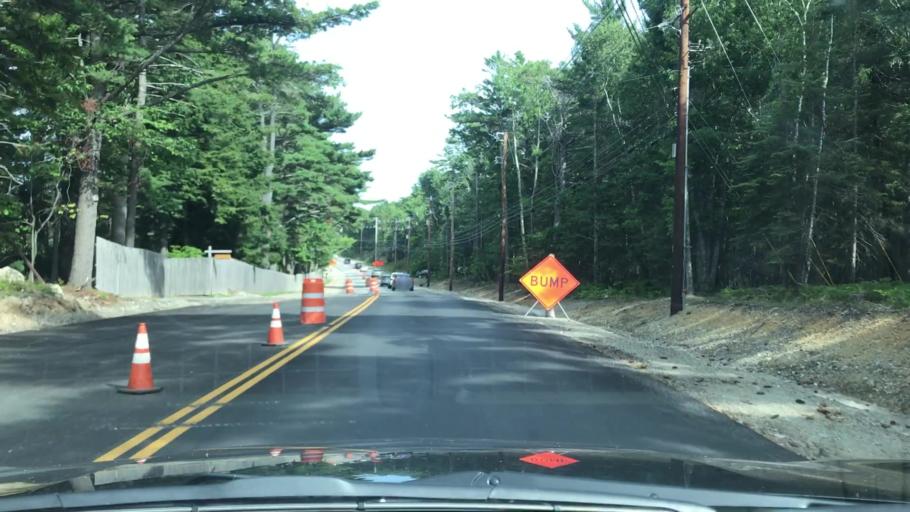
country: US
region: Maine
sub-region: Hancock County
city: Bar Harbor
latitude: 44.4102
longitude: -68.2457
